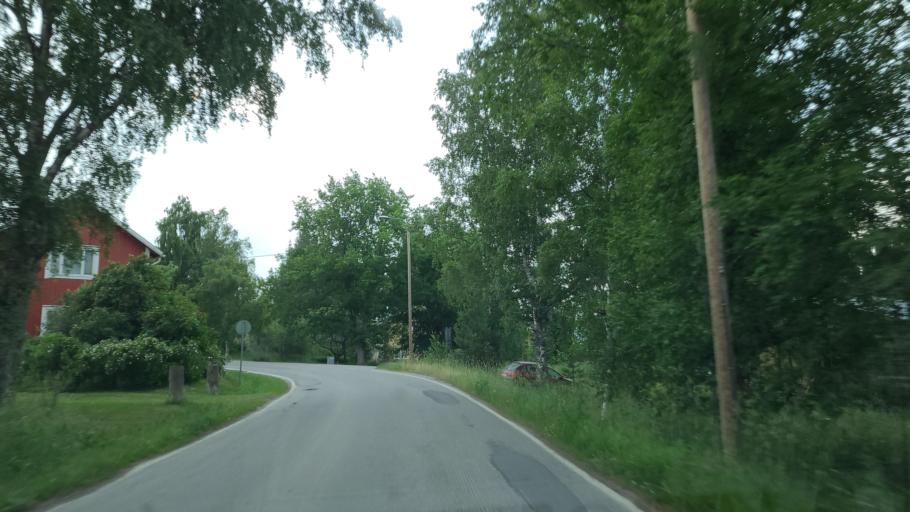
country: FI
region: Ostrobothnia
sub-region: Vaasa
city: Replot
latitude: 63.1801
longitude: 21.2815
